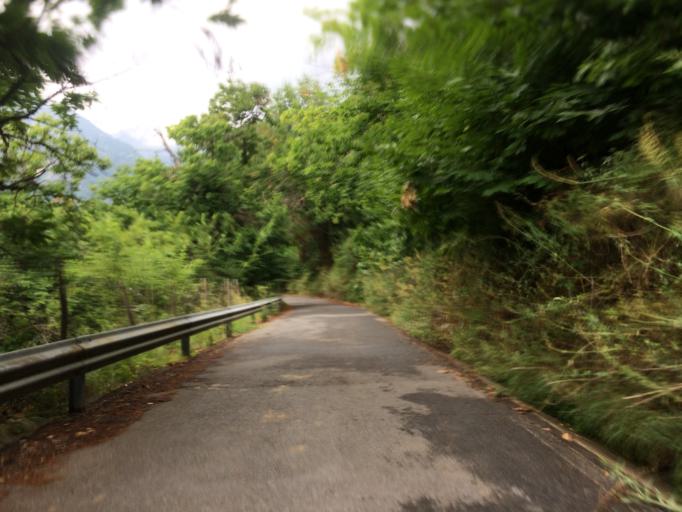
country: IT
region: Liguria
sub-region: Provincia di Imperia
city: Castel Vittorio
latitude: 43.9434
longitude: 7.6903
